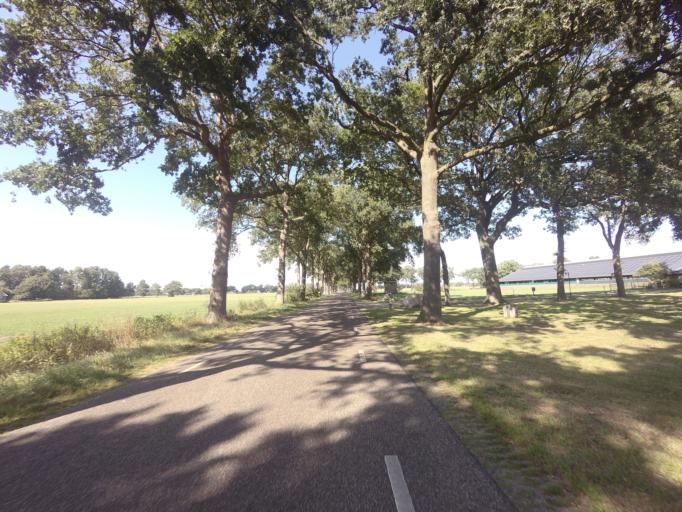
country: NL
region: Drenthe
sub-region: Gemeente Hoogeveen
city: Hoogeveen
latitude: 52.6237
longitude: 6.4820
